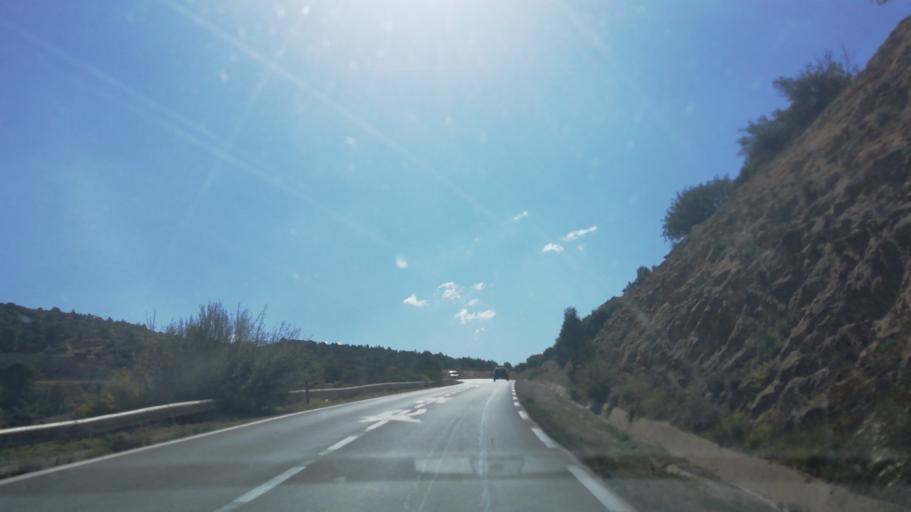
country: DZ
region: Mascara
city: Mascara
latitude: 35.4855
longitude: 0.1522
